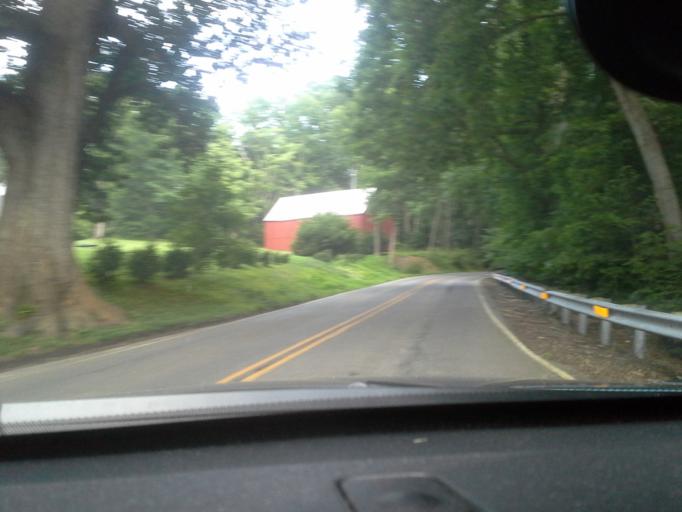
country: US
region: Maryland
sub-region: Calvert County
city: Huntingtown
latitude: 38.6050
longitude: -76.5480
